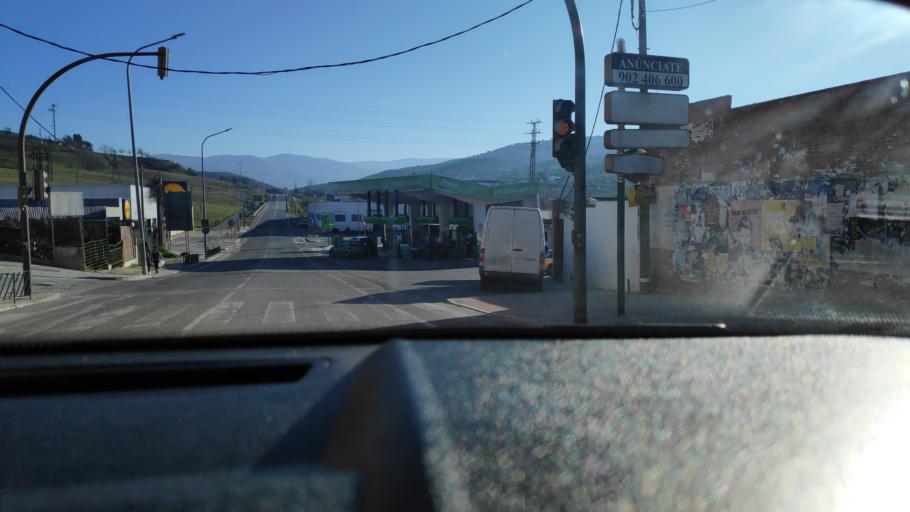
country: ES
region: Andalusia
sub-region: Province of Cordoba
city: Baena
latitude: 37.6129
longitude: -4.3213
